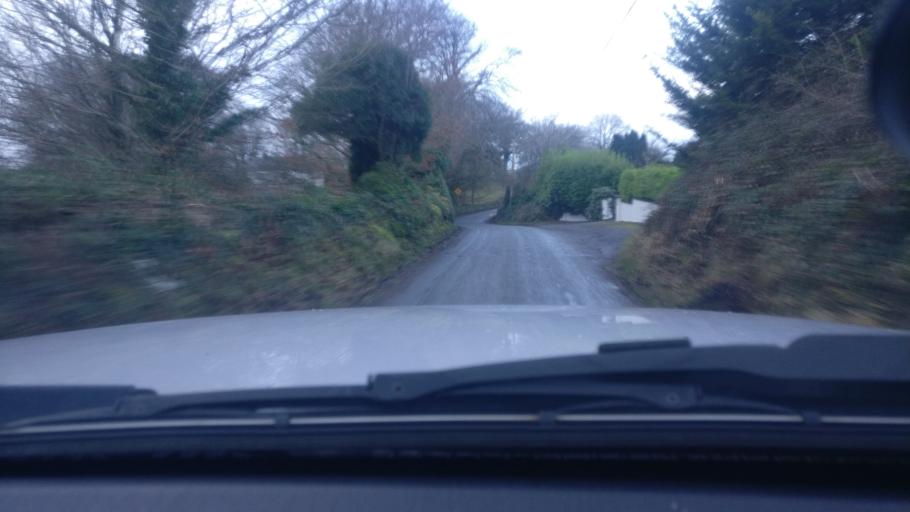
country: IE
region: Connaught
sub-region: County Galway
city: Loughrea
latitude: 53.1647
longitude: -8.5784
